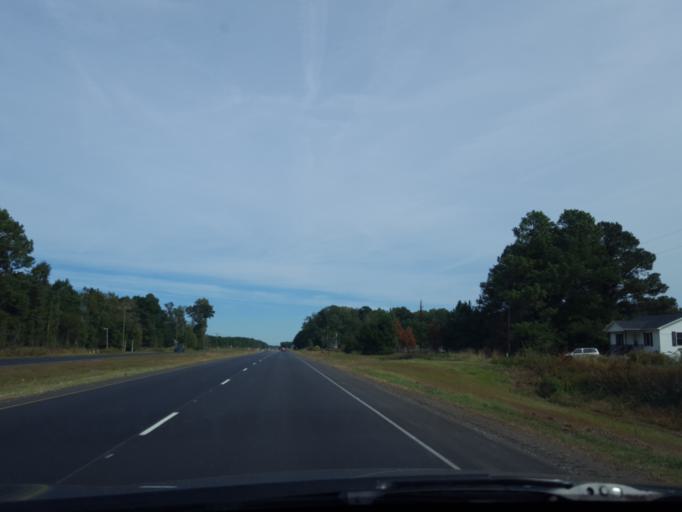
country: US
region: North Carolina
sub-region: Chowan County
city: Edenton
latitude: 36.1077
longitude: -76.5233
